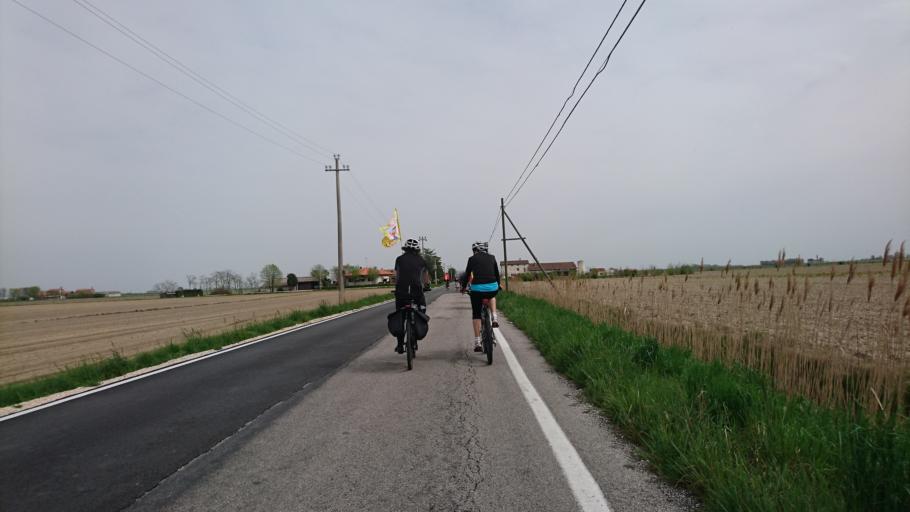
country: IT
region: Veneto
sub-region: Provincia di Venezia
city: La Salute di Livenza
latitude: 45.6586
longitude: 12.8353
